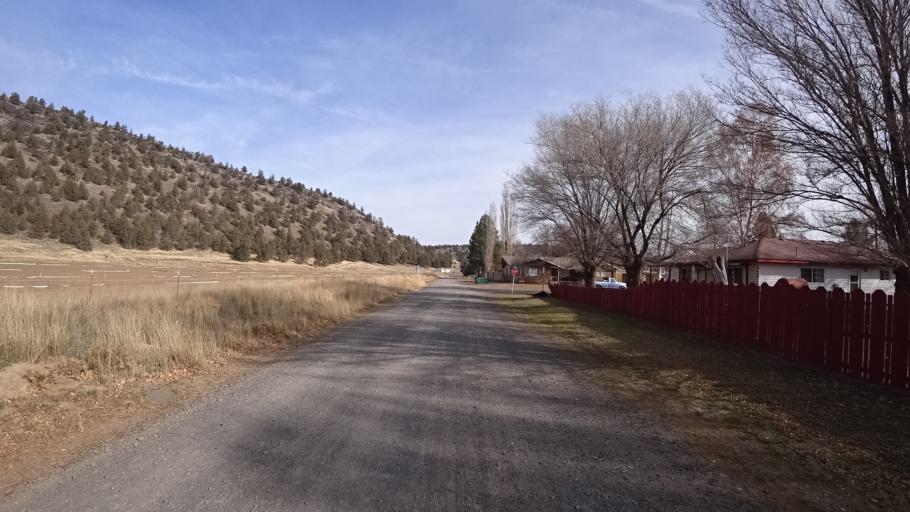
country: US
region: Oregon
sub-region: Klamath County
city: Klamath Falls
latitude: 41.9716
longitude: -121.9175
